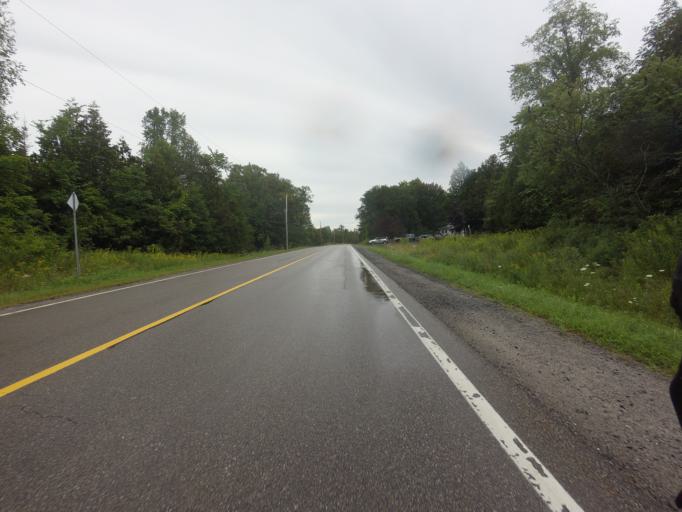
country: CA
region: Ontario
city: Perth
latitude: 44.9751
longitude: -76.4058
